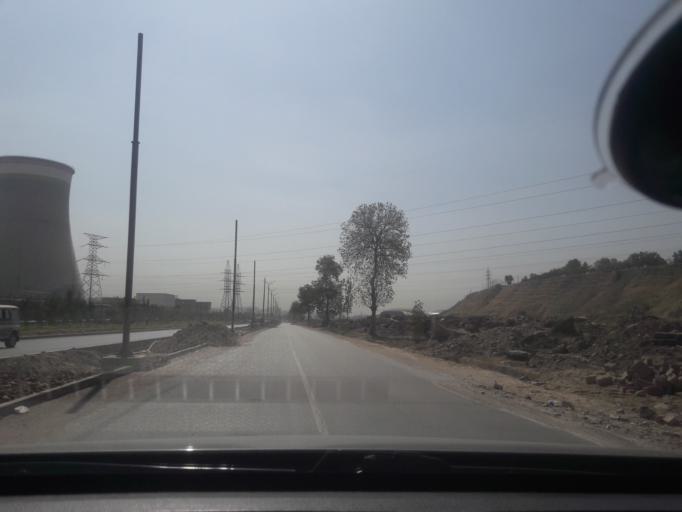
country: TJ
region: Dushanbe
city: Dushanbe
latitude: 38.6107
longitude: 68.7705
